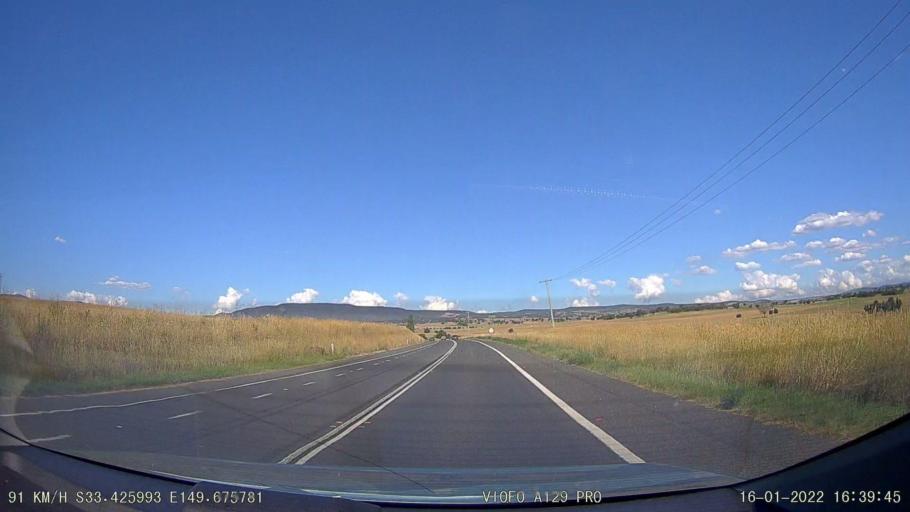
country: AU
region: New South Wales
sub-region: Bathurst Regional
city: Kelso
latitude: -33.4259
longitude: 149.6758
